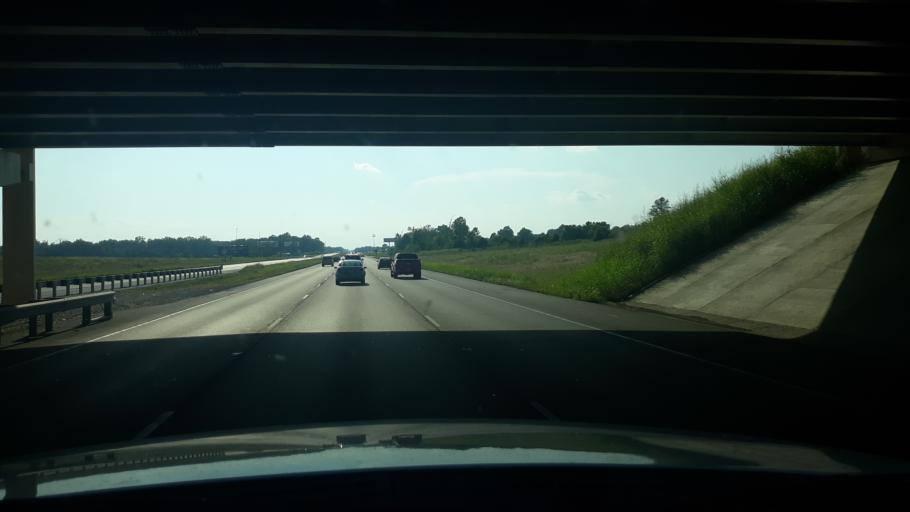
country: US
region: Illinois
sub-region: Williamson County
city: Crainville
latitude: 37.7452
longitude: -89.0578
